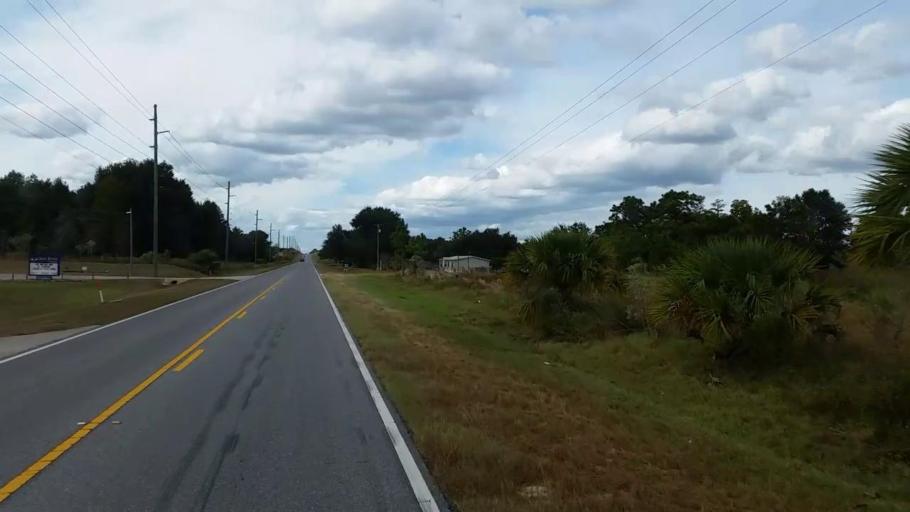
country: US
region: Florida
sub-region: Lake County
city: Four Corners
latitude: 28.3702
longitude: -81.6930
